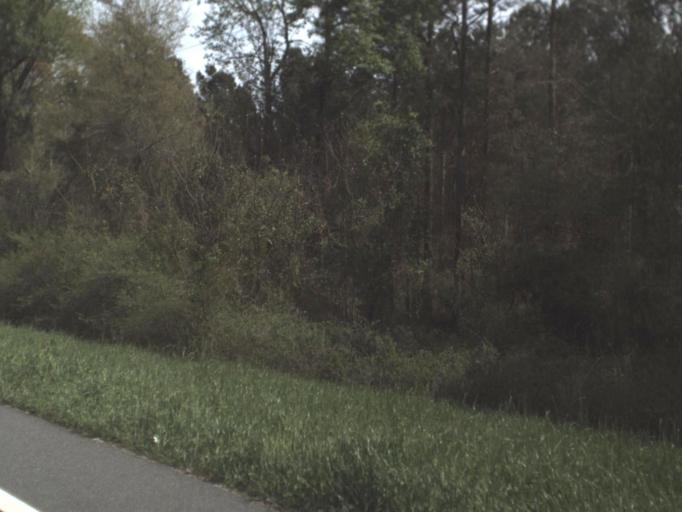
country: US
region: Alabama
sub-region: Houston County
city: Cottonwood
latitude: 30.9448
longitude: -85.2729
